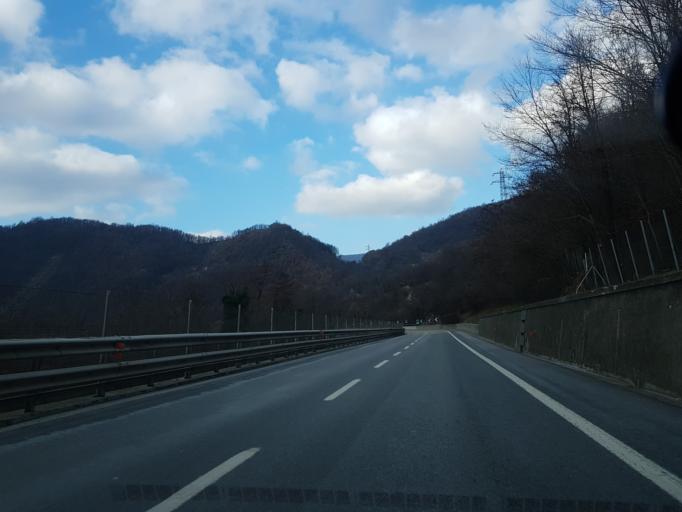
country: IT
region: Liguria
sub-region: Provincia di Genova
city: Isola del Cantone
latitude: 44.6485
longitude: 8.9593
